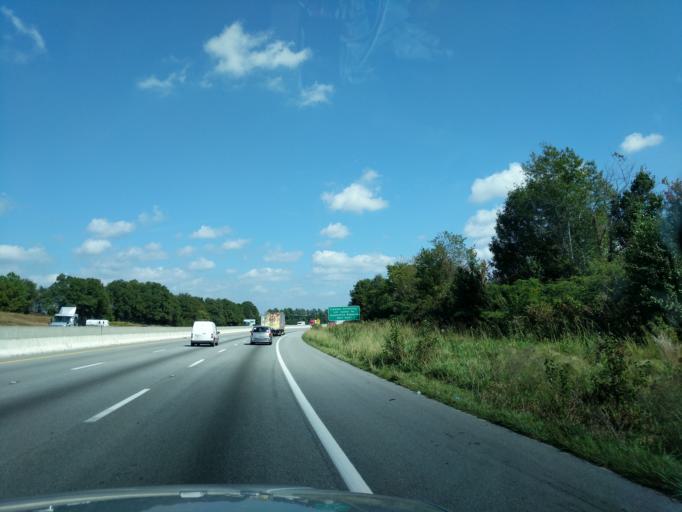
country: US
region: South Carolina
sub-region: Greenville County
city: Mauldin
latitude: 34.8104
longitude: -82.3438
